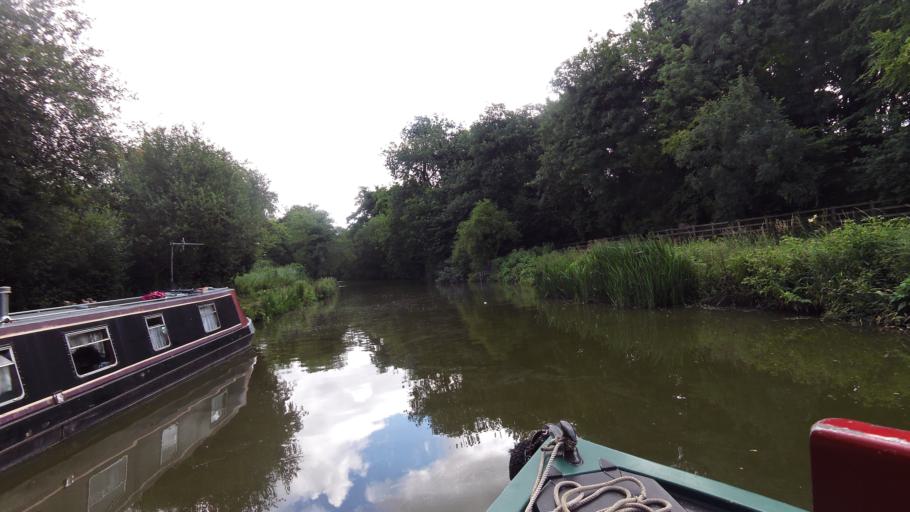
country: GB
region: England
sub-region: West Berkshire
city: Kintbury
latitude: 51.4021
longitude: -1.4405
